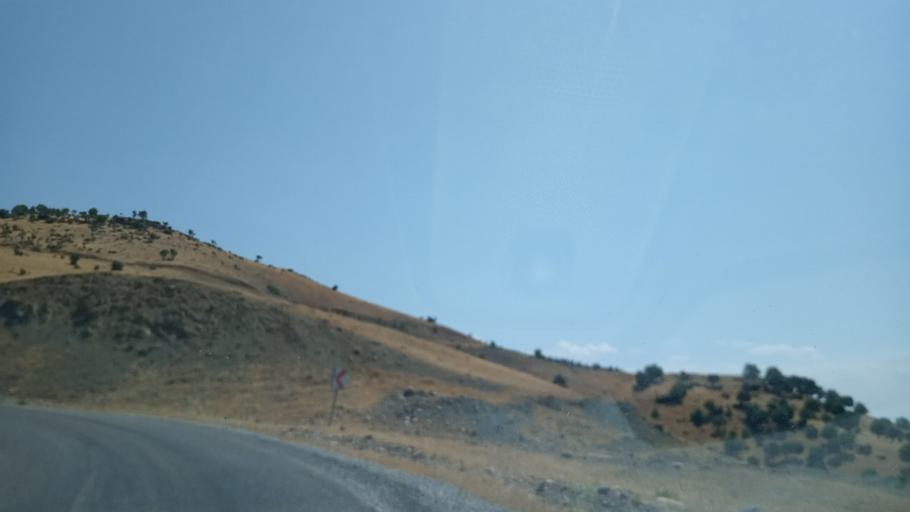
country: TR
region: Siirt
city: Dilektepe
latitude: 38.0690
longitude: 41.8291
